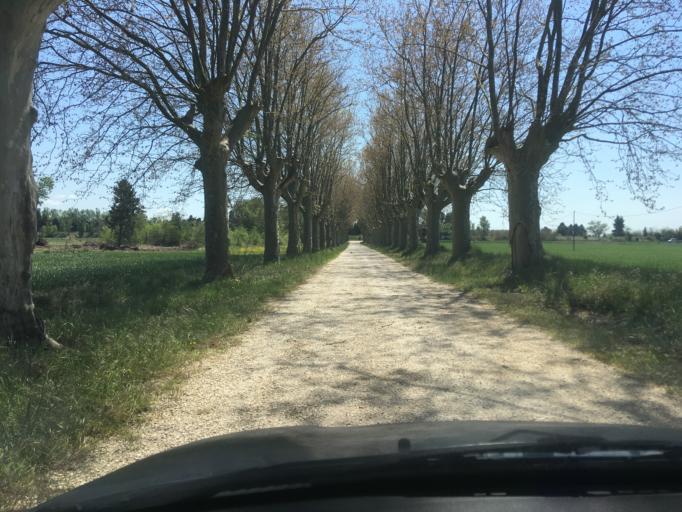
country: FR
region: Provence-Alpes-Cote d'Azur
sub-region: Departement du Vaucluse
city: Althen-des-Paluds
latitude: 44.0387
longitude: 4.9524
